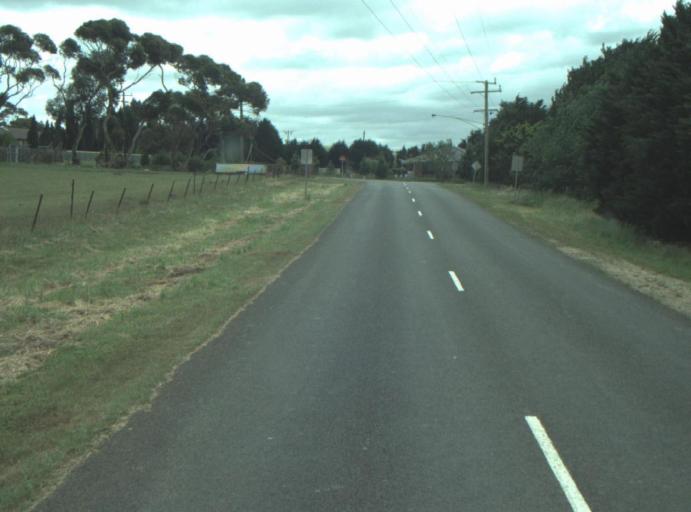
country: AU
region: Victoria
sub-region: Greater Geelong
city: Bell Post Hill
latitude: -38.0475
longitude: 144.3437
